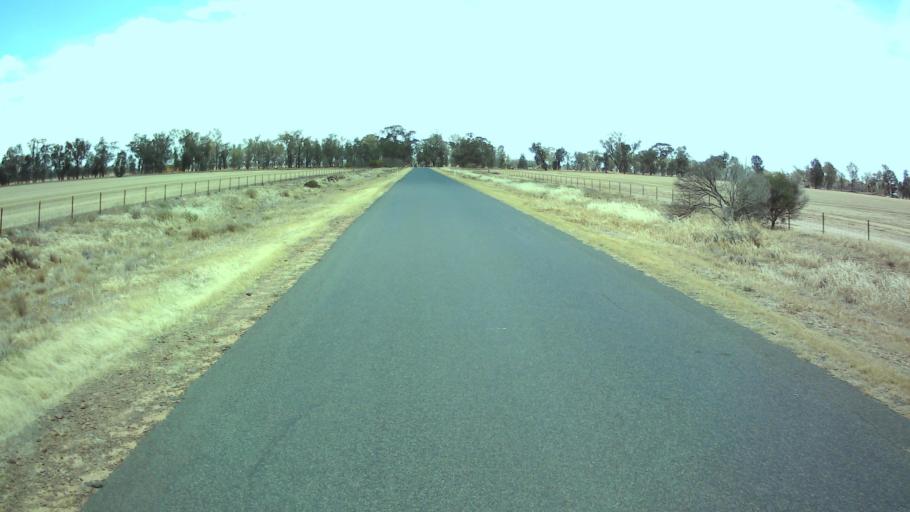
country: AU
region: New South Wales
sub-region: Weddin
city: Grenfell
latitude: -34.0727
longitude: 147.7771
